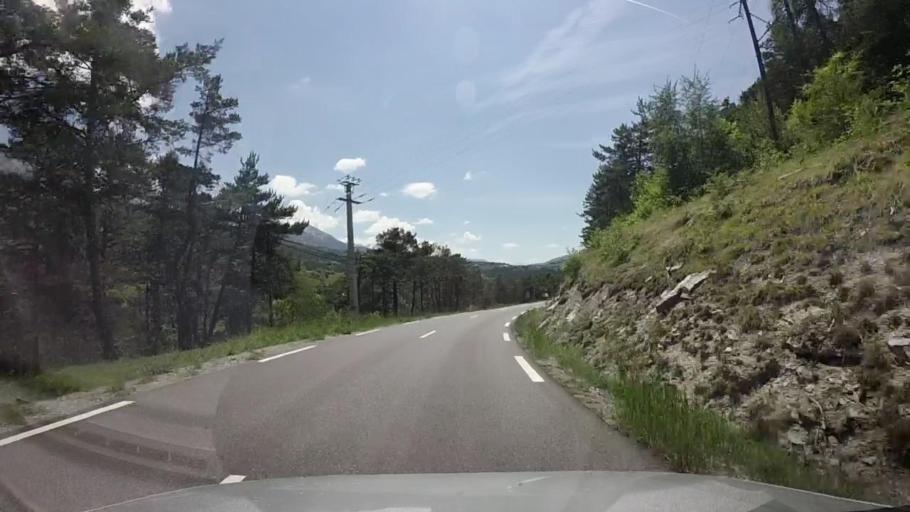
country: FR
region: Provence-Alpes-Cote d'Azur
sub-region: Departement des Alpes-de-Haute-Provence
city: Seyne-les-Alpes
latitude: 44.4029
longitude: 6.3324
